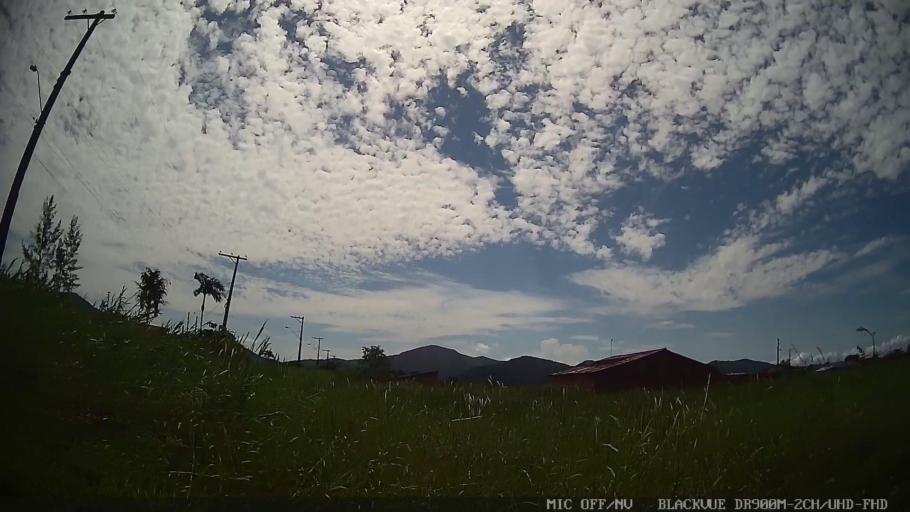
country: BR
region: Sao Paulo
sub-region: Iguape
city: Iguape
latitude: -24.7198
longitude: -47.5074
